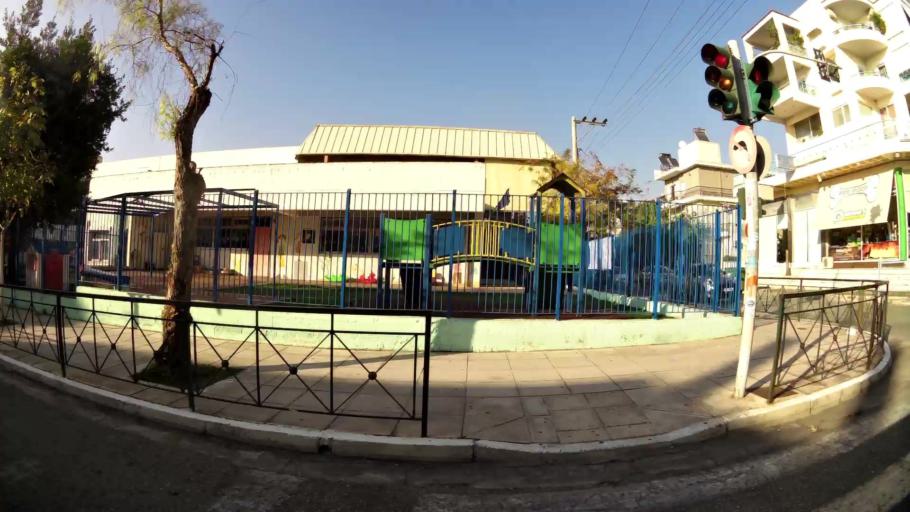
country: GR
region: Attica
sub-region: Nomarchia Athinas
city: Argyroupoli
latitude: 37.8951
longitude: 23.7529
